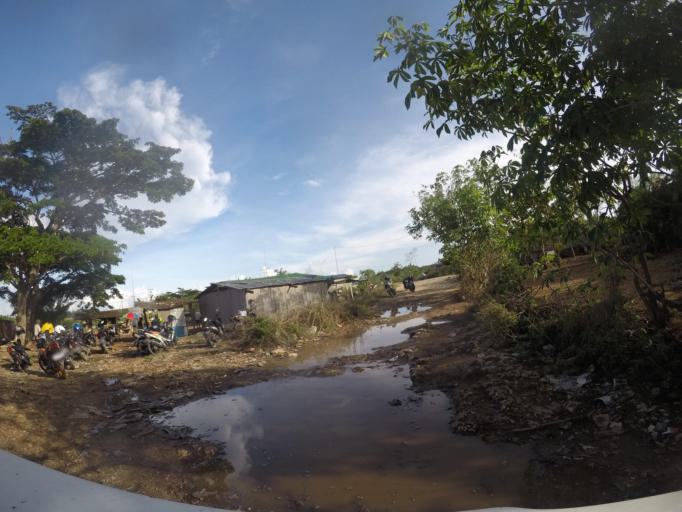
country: TL
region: Baucau
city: Baucau
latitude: -8.4859
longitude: 126.4534
